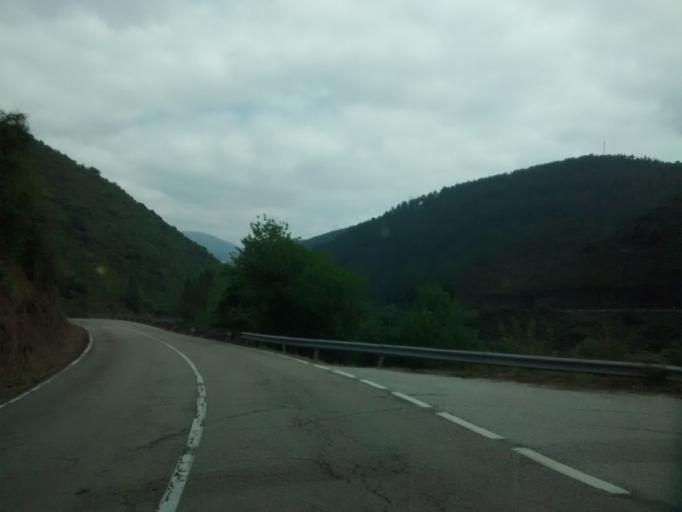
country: ES
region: Galicia
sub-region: Provincia de Ourense
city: Manzaneda
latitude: 42.3276
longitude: -7.2128
